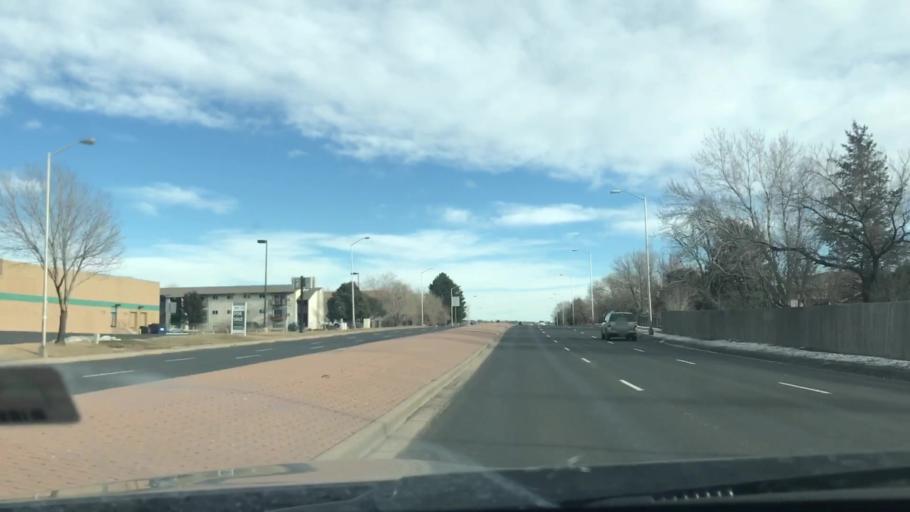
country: US
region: Colorado
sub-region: El Paso County
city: Colorado Springs
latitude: 38.9037
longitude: -104.7736
